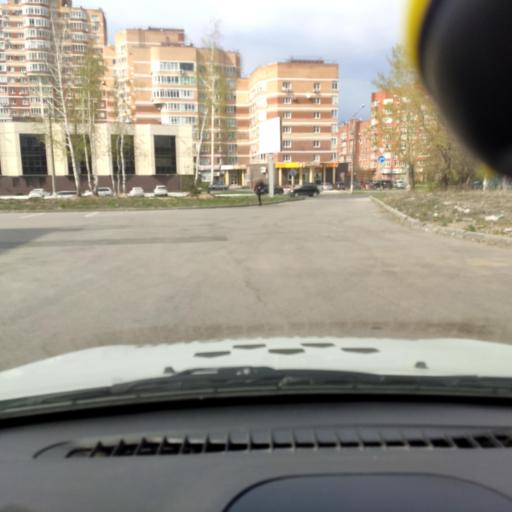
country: RU
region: Samara
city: Tol'yatti
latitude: 53.5005
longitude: 49.4233
